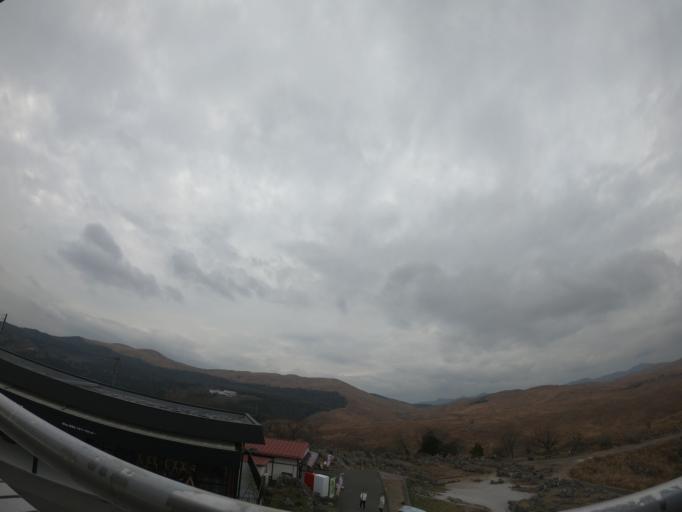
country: JP
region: Yamaguchi
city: Ogori-shimogo
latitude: 34.2349
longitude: 131.3058
